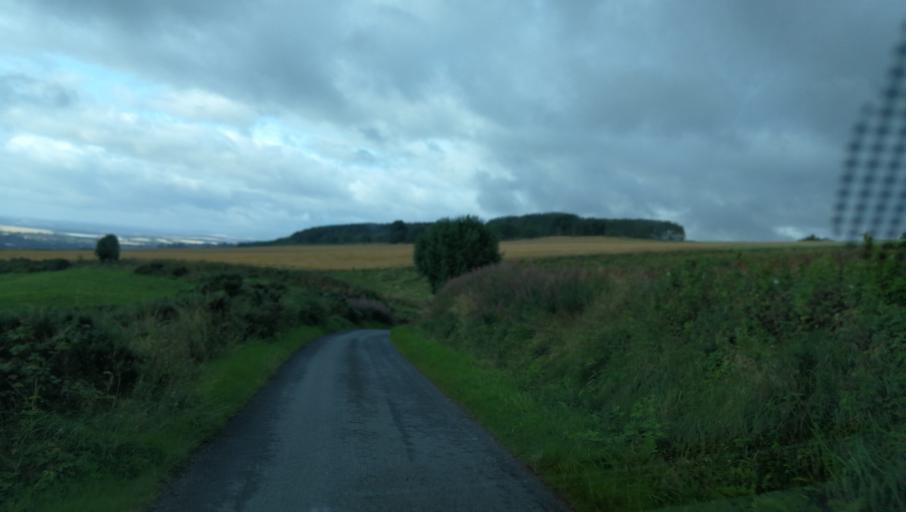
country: GB
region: Scotland
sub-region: Perth and Kinross
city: Alyth
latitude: 56.6171
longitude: -3.2864
